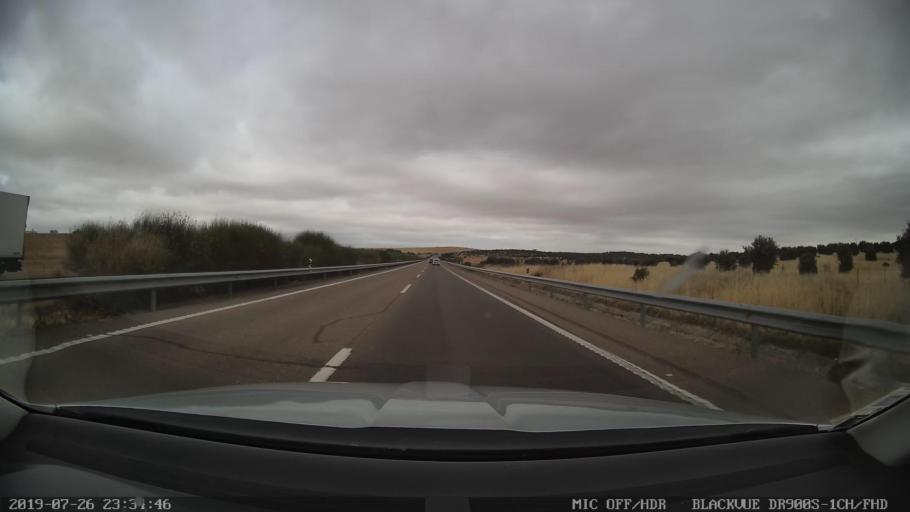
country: ES
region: Extremadura
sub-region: Provincia de Caceres
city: Santa Cruz de la Sierra
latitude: 39.3651
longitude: -5.8714
